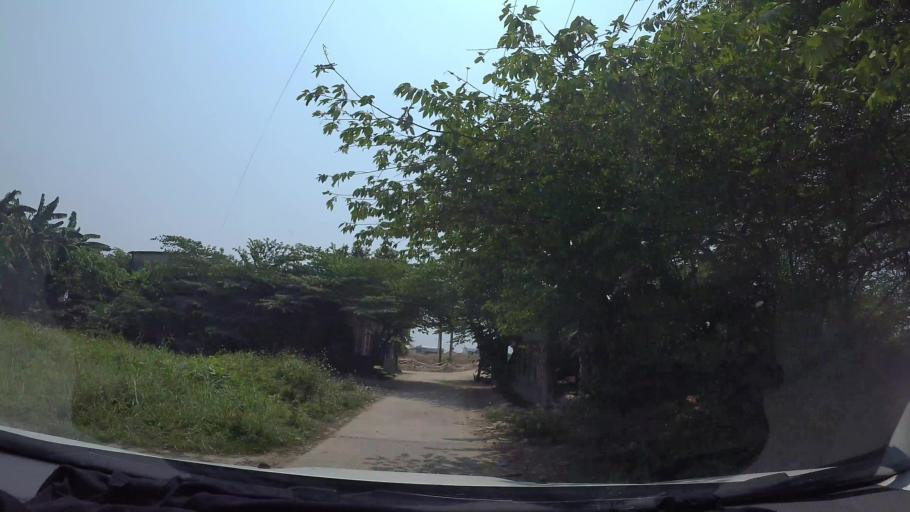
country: VN
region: Da Nang
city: Cam Le
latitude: 16.0174
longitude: 108.2236
